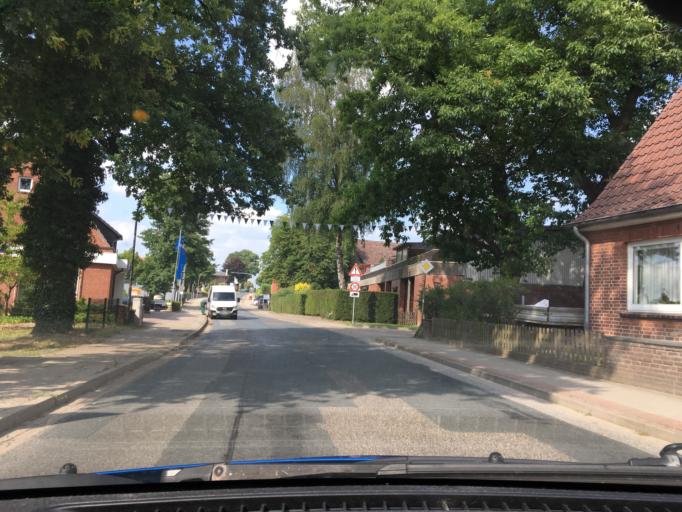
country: DE
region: Lower Saxony
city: Bendestorf
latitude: 53.3691
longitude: 9.9381
